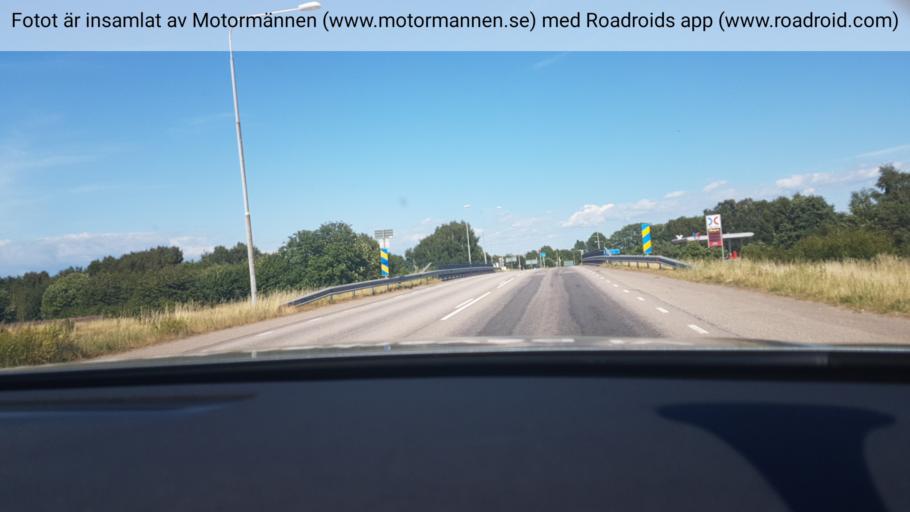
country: SE
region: Halland
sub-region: Falkenbergs Kommun
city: Falkenberg
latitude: 56.8984
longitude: 12.5279
